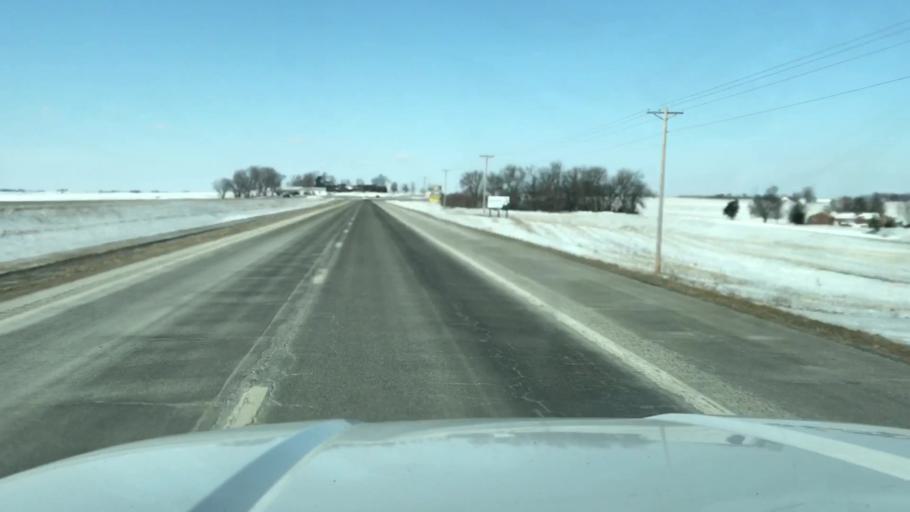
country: US
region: Missouri
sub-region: Nodaway County
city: Maryville
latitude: 40.2745
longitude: -94.8695
